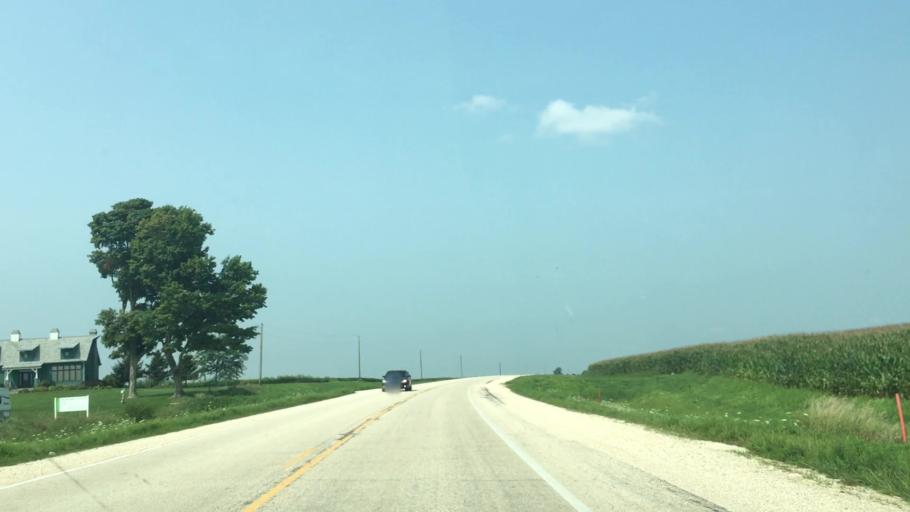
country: US
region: Iowa
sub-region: Fayette County
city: West Union
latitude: 42.9806
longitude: -91.8240
